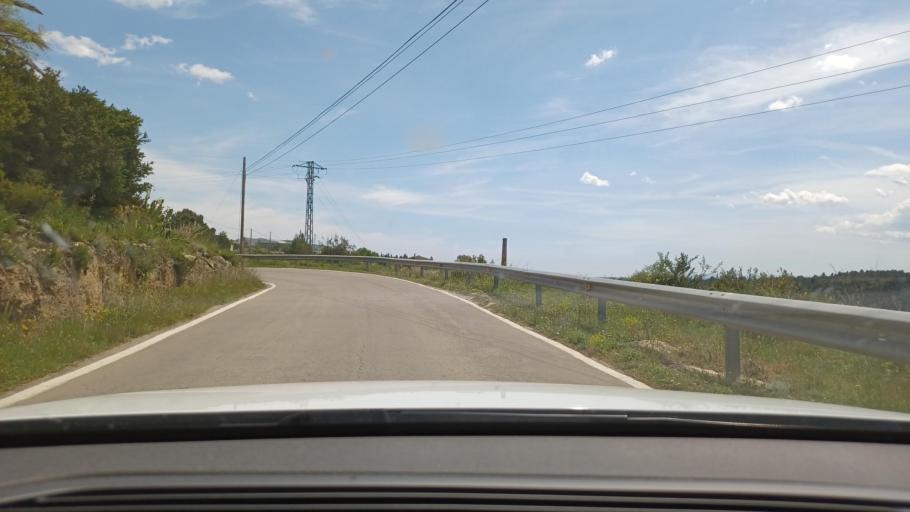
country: ES
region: Valencia
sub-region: Provincia de Castello
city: Rosell
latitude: 40.6455
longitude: 0.2700
